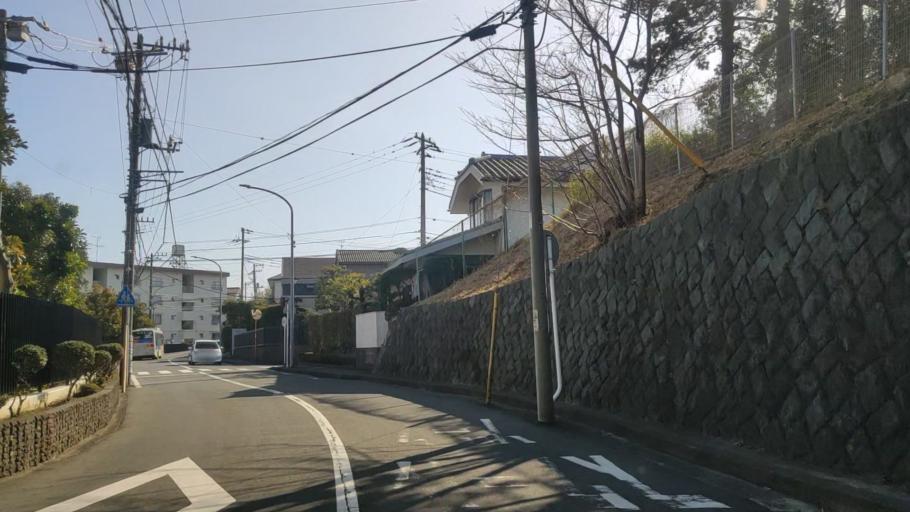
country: JP
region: Kanagawa
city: Yokohama
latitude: 35.4687
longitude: 139.5969
